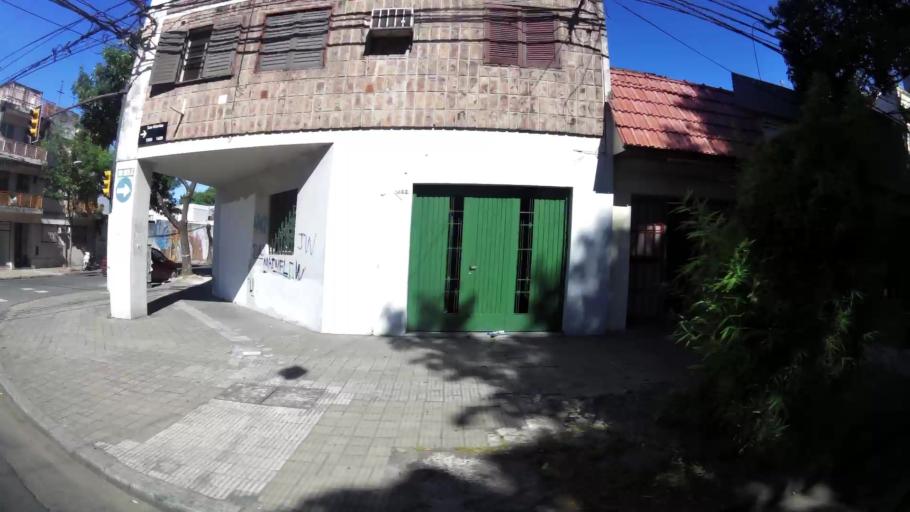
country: AR
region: Santa Fe
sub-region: Departamento de Rosario
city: Rosario
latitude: -32.9487
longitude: -60.6745
